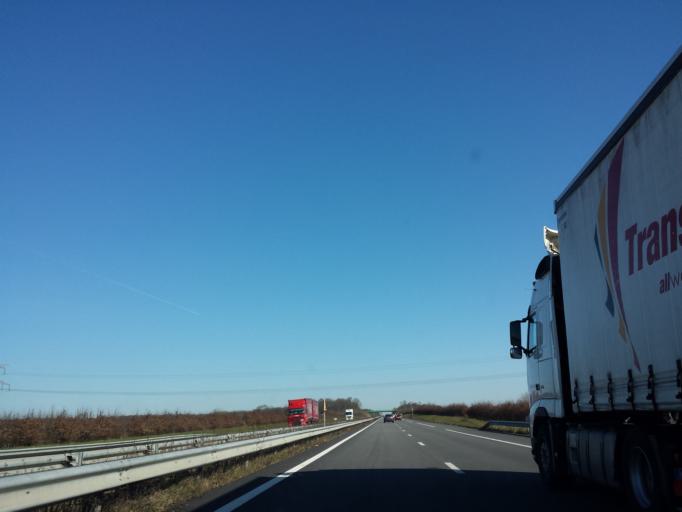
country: FR
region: Picardie
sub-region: Departement de l'Oise
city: Saint-Crepin-Ibouvillers
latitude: 49.3071
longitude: 2.0777
